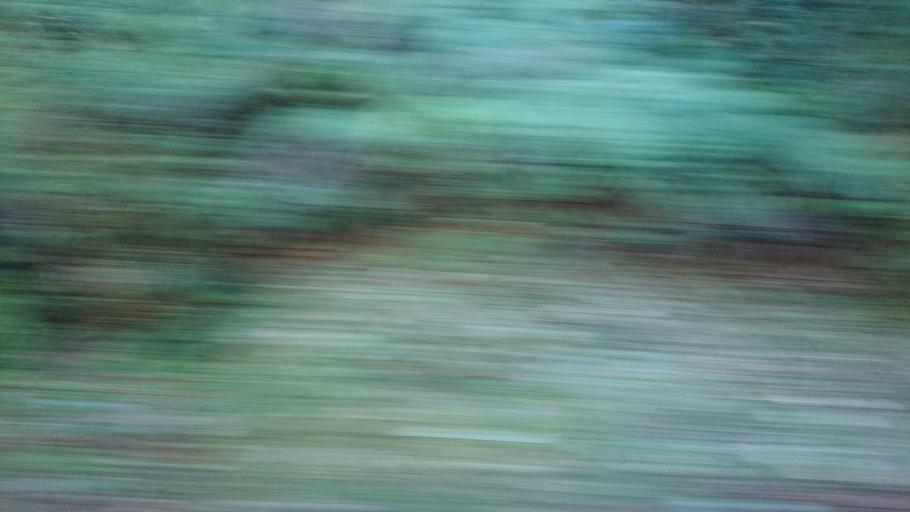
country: TW
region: Taiwan
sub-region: Hualien
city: Hualian
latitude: 24.3713
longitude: 121.3397
